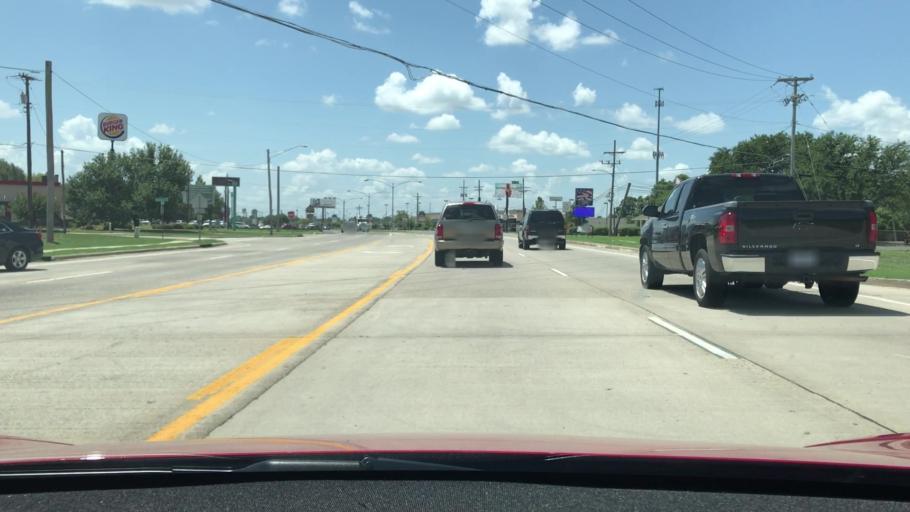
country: US
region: Louisiana
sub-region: Bossier Parish
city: Bossier City
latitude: 32.4513
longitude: -93.7222
